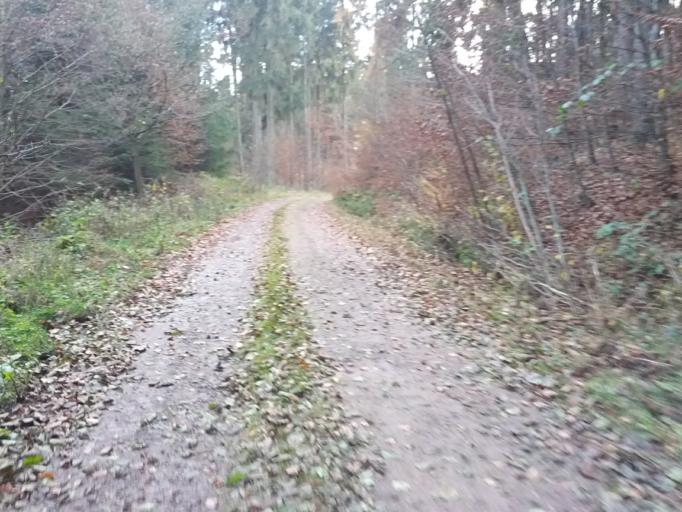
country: DE
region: Thuringia
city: Eisenach
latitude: 50.9476
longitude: 10.3449
